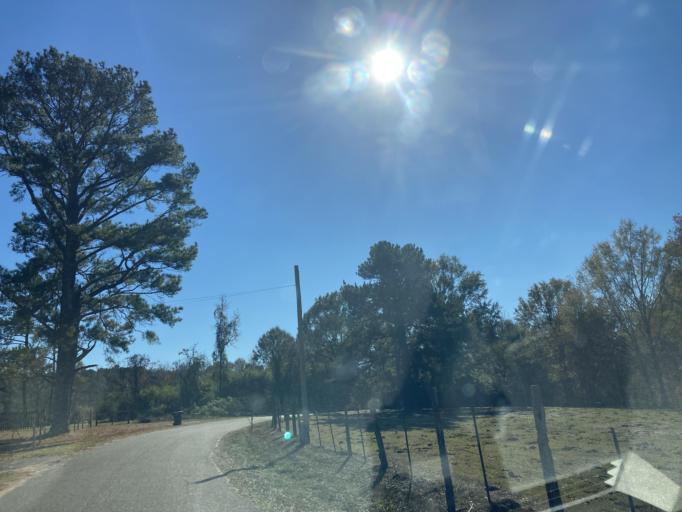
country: US
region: Mississippi
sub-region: Lamar County
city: Sumrall
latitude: 31.2962
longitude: -89.6455
